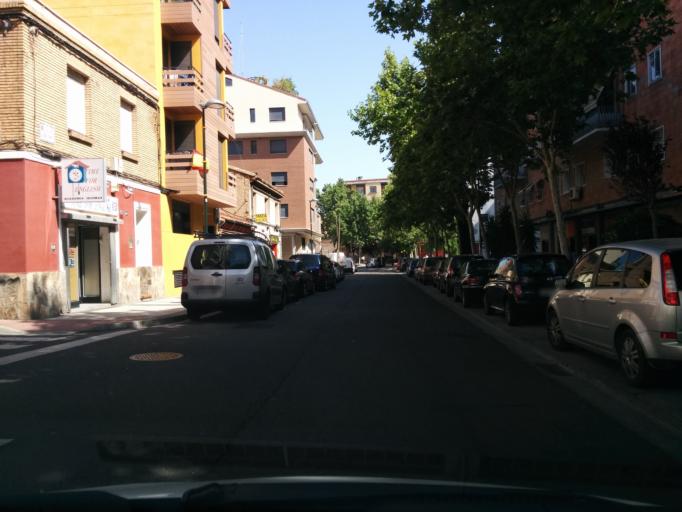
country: ES
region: Aragon
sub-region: Provincia de Zaragoza
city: Zaragoza
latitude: 41.6310
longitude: -0.8842
